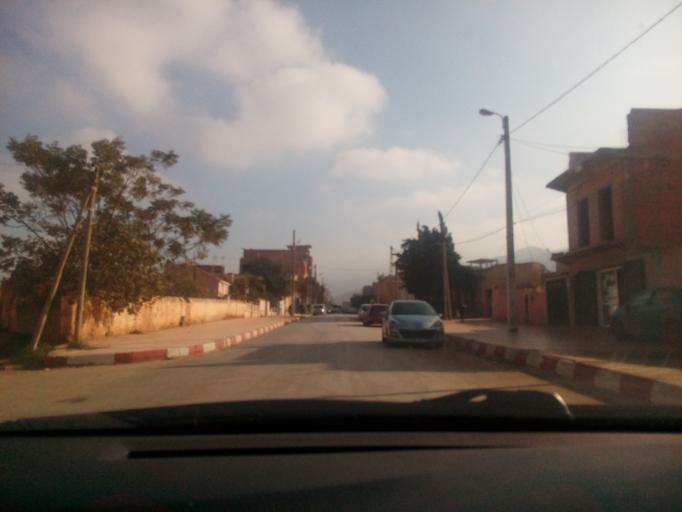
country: DZ
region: Oran
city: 'Ain el Turk
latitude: 35.7024
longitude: -0.8178
